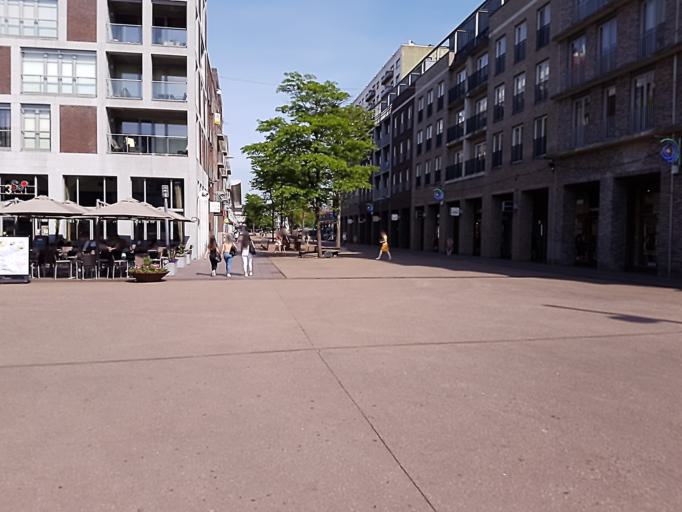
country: BE
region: Flanders
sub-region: Provincie Limburg
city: Genk
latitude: 50.9653
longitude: 5.4957
